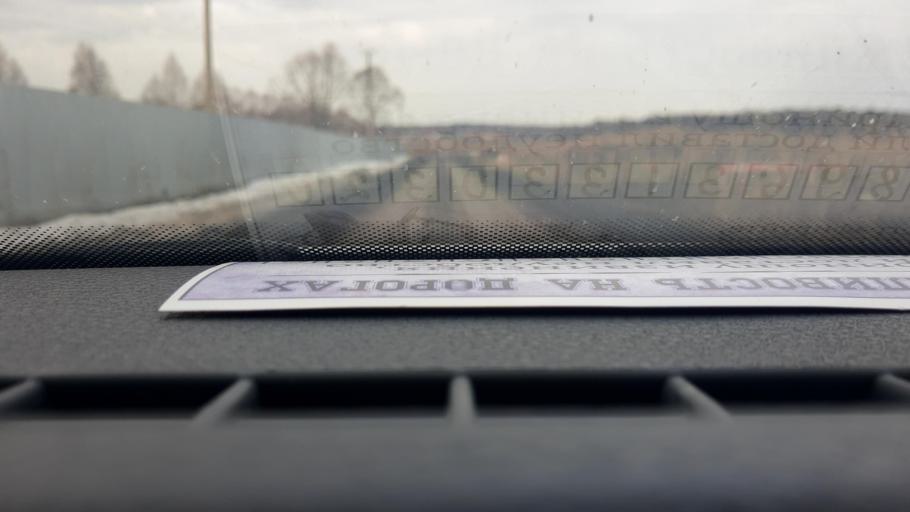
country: RU
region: Bashkortostan
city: Mikhaylovka
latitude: 54.7398
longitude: 55.8156
